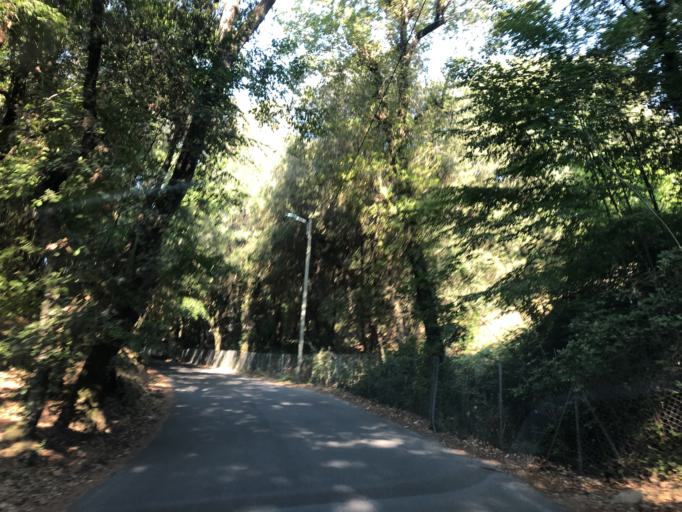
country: FR
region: Provence-Alpes-Cote d'Azur
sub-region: Departement des Alpes-Maritimes
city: Biot
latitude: 43.6229
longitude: 7.0916
